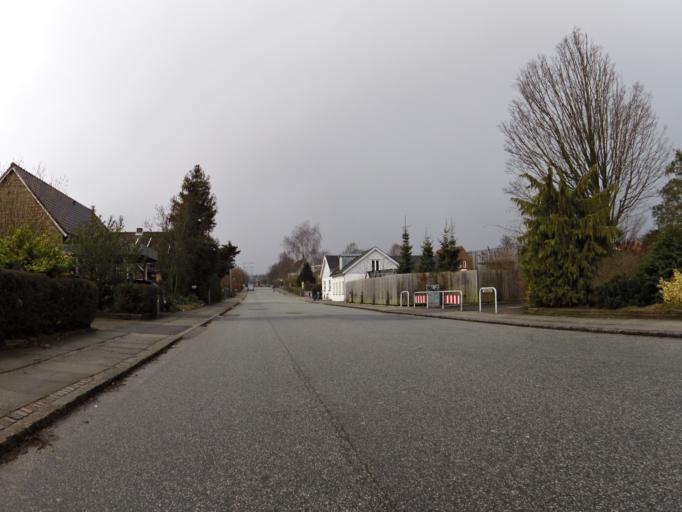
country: DK
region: Central Jutland
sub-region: Arhus Kommune
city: Arhus
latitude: 56.1663
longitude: 10.1810
